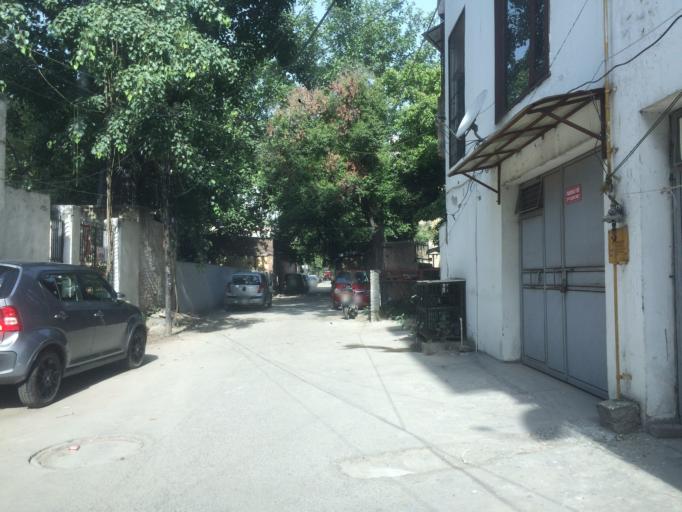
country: IN
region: NCT
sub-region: New Delhi
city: New Delhi
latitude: 28.5660
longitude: 77.2482
